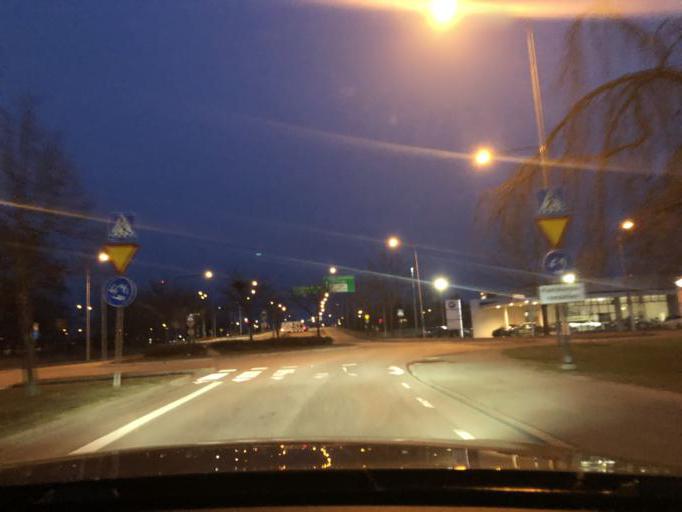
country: SE
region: Kalmar
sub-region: Kalmar Kommun
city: Kalmar
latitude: 56.6754
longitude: 16.3213
